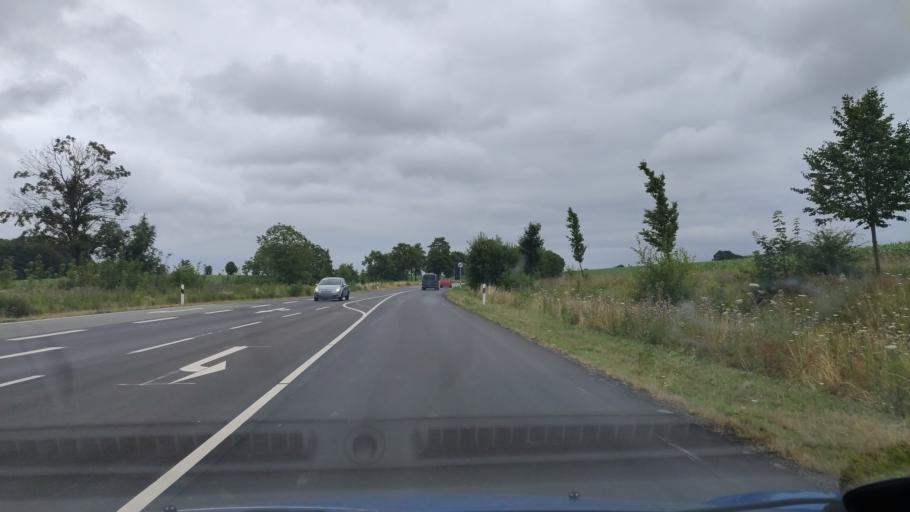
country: DE
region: Lower Saxony
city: Bad Munder am Deister
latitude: 52.2225
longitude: 9.4356
